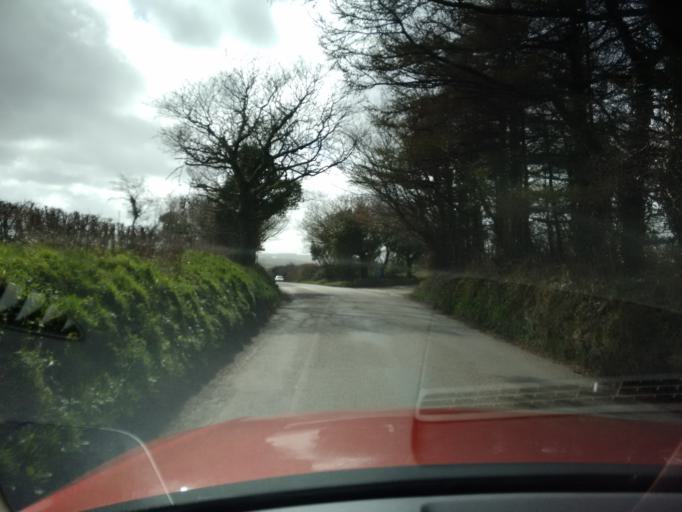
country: GB
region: England
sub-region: Cornwall
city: Liskeard
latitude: 50.4814
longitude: -4.5130
